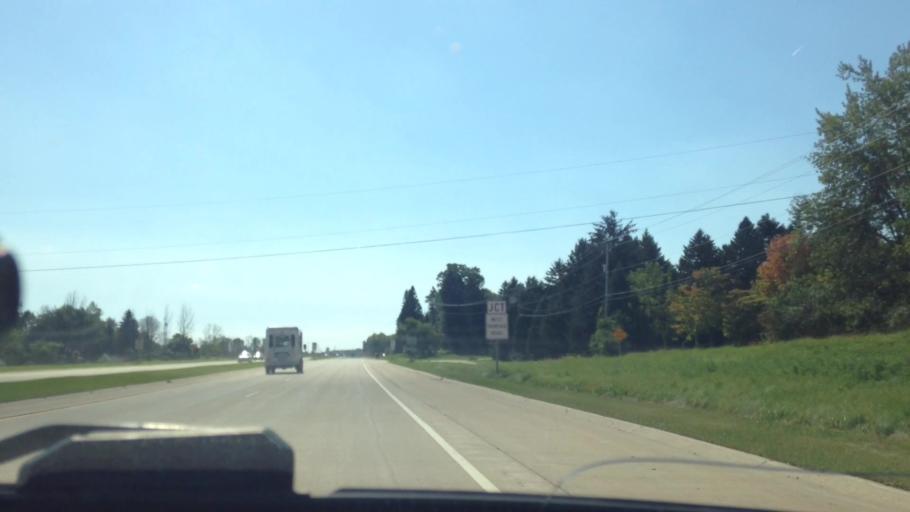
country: US
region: Wisconsin
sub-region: Ozaukee County
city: Saukville
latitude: 43.3513
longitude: -87.9152
